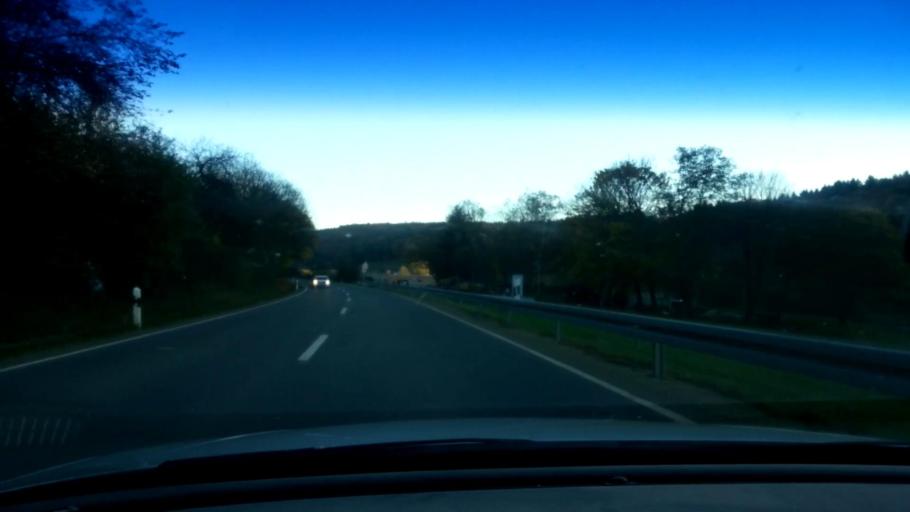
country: DE
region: Bavaria
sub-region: Upper Franconia
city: Heiligenstadt
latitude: 49.8538
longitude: 11.1812
